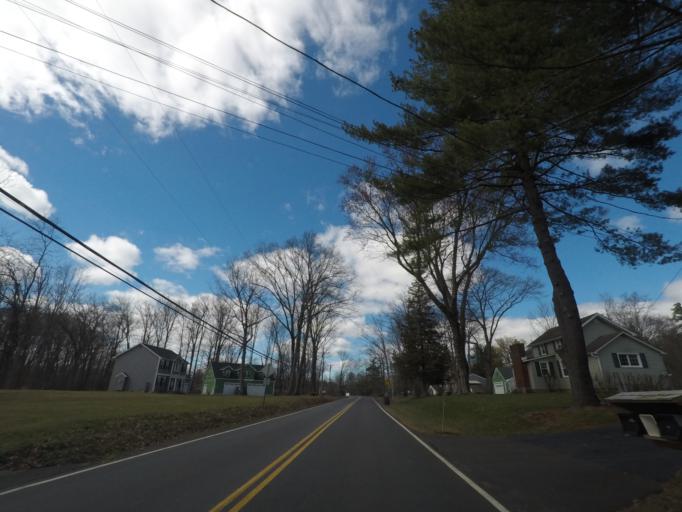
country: US
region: New York
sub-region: Albany County
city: Delmar
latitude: 42.5731
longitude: -73.8259
